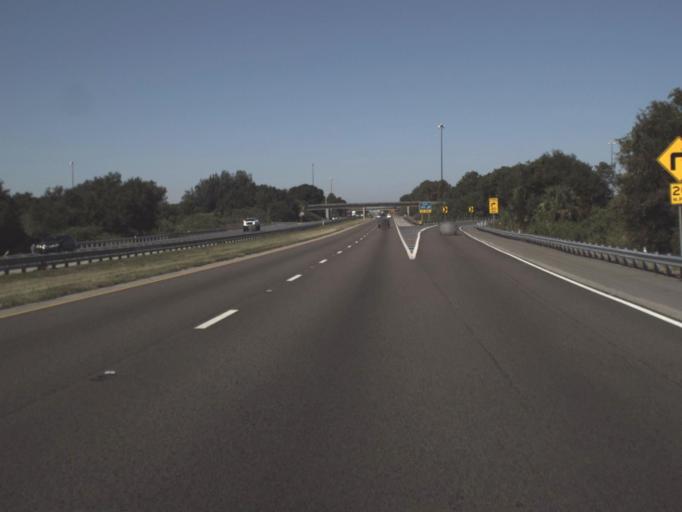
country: US
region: Florida
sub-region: Lake County
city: Howie In The Hills
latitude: 28.6498
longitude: -81.8029
